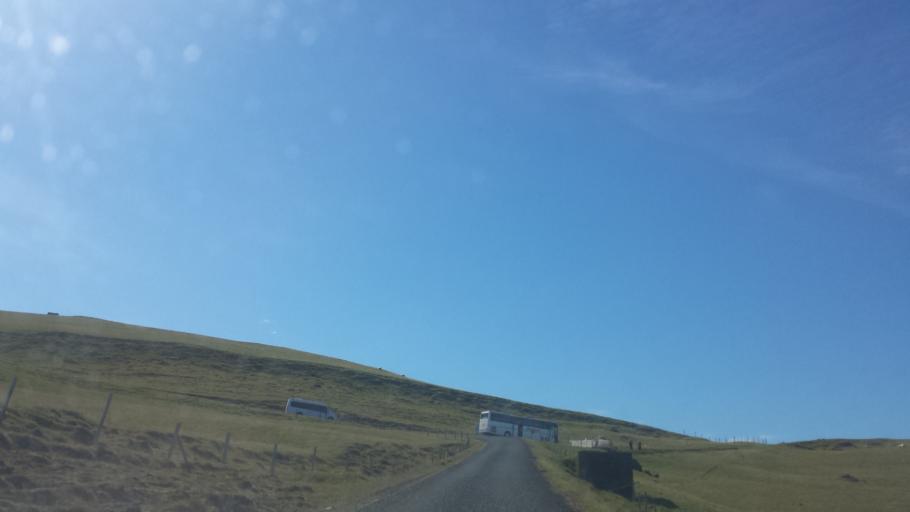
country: IS
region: South
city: Vestmannaeyjar
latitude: 63.4036
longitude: -20.2817
